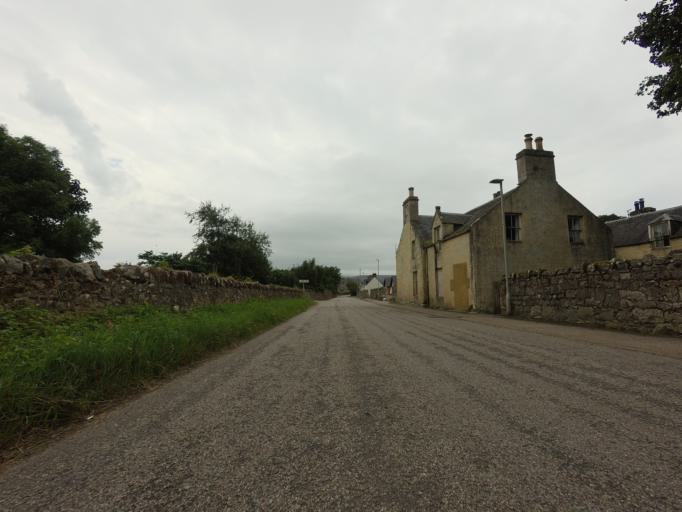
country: GB
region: Scotland
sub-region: Highland
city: Alness
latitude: 57.8838
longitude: -4.3651
